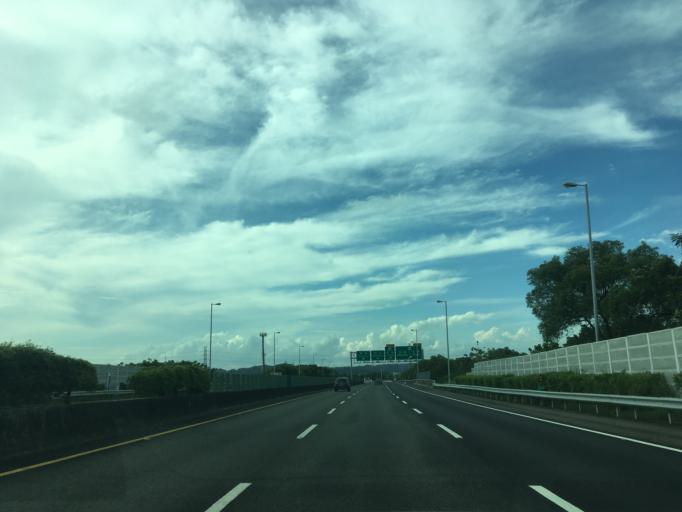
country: TW
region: Taiwan
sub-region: Chiayi
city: Jiayi Shi
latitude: 23.4932
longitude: 120.4945
